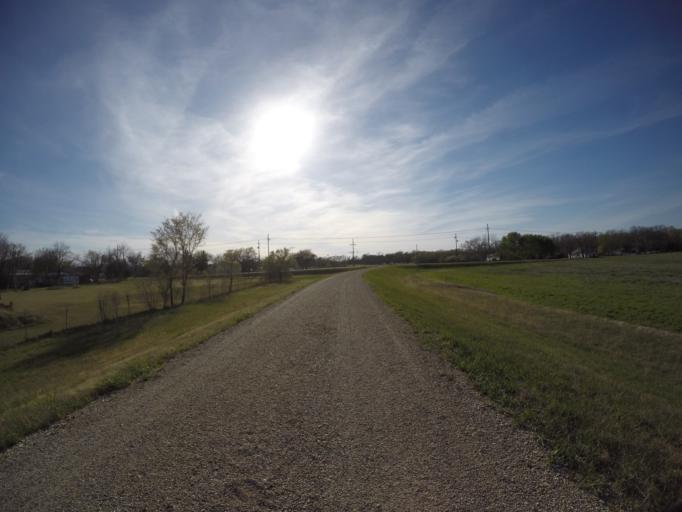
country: US
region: Kansas
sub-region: Saline County
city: Salina
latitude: 38.8649
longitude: -97.6066
